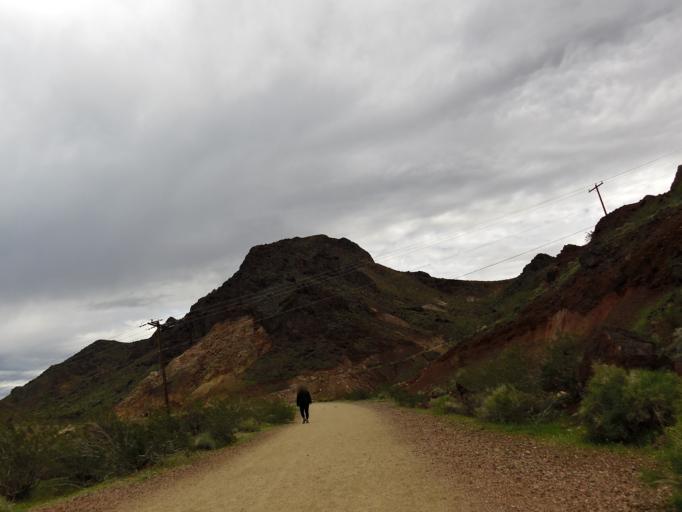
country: US
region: Nevada
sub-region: Clark County
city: Boulder City
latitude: 36.0133
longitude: -114.7846
